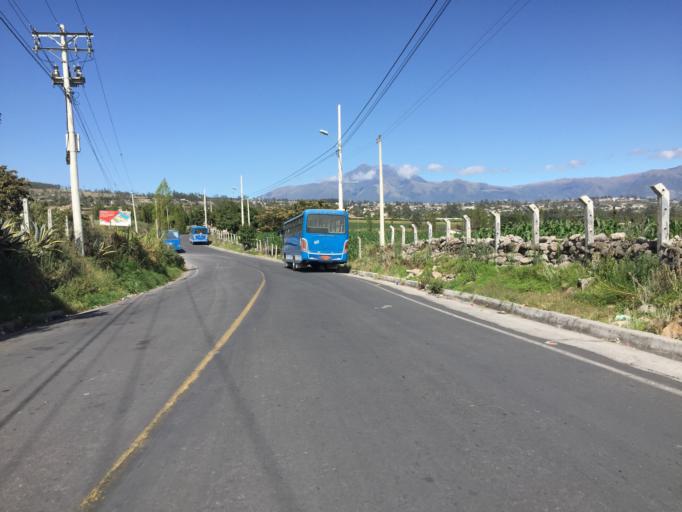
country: EC
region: Imbabura
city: Ibarra
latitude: 0.3171
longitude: -78.1469
